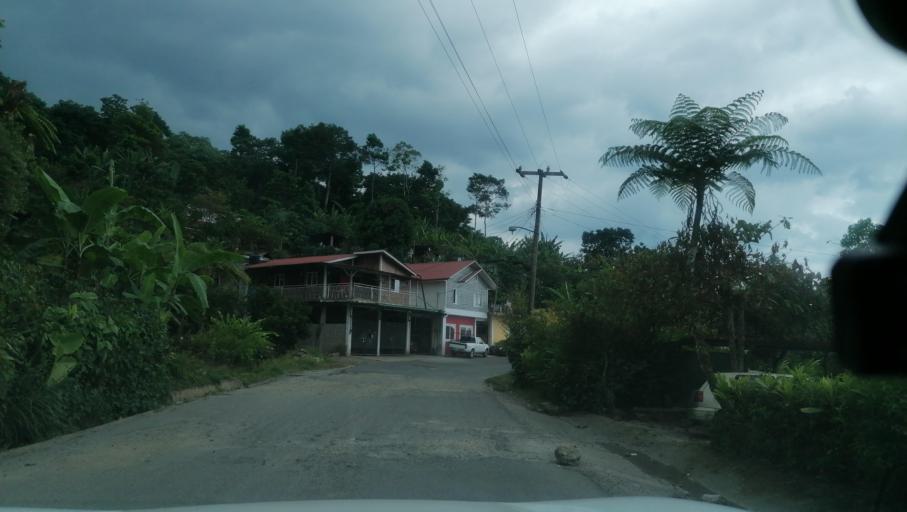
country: MX
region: Chiapas
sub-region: Cacahoatan
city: Benito Juarez
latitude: 15.0854
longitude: -92.1965
